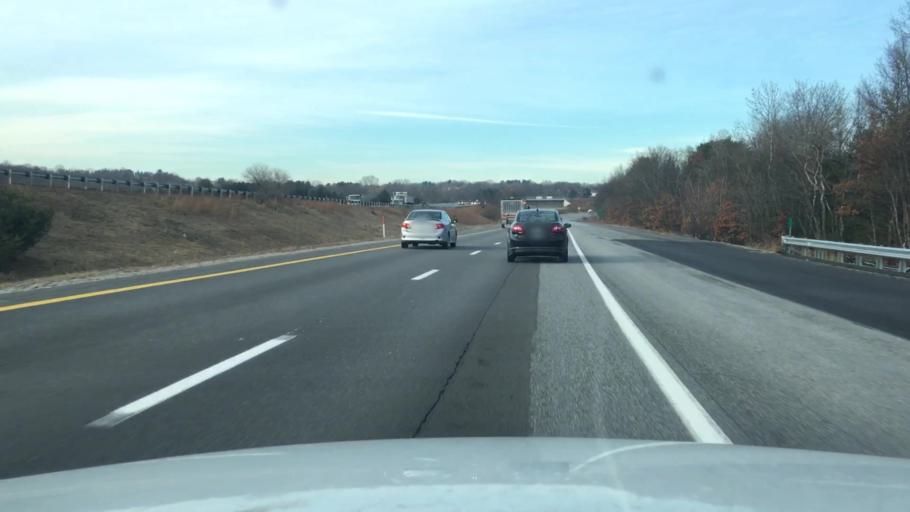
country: US
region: New Hampshire
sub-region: Hillsborough County
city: Manchester
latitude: 42.9626
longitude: -71.4100
